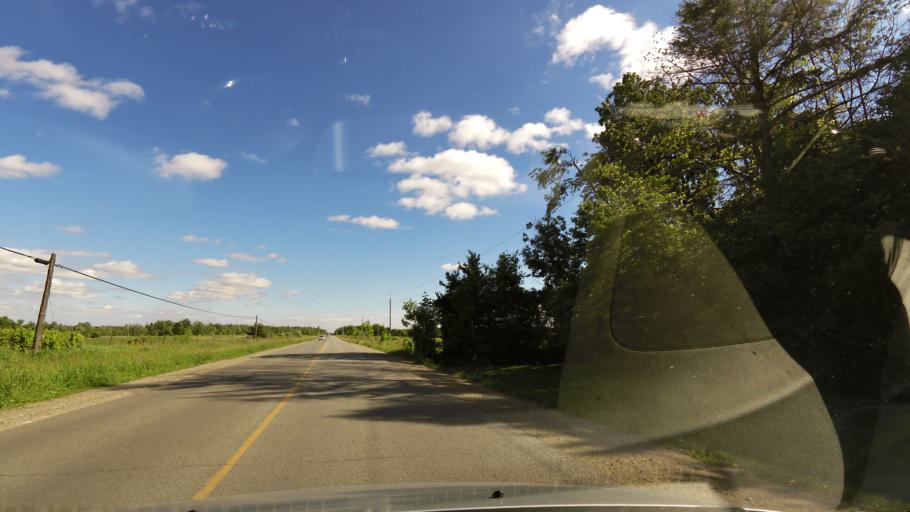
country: CA
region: Ontario
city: Bradford West Gwillimbury
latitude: 44.1596
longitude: -79.6155
